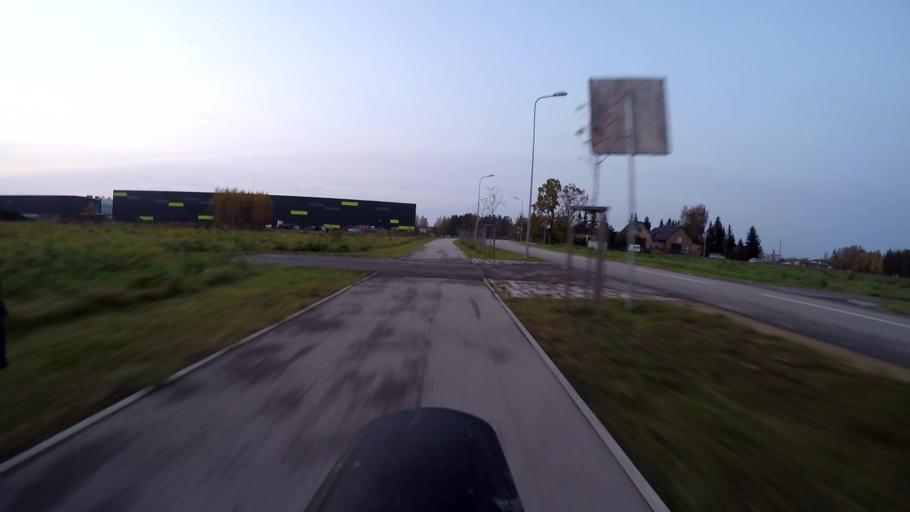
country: LV
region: Marupe
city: Marupe
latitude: 56.9158
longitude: 23.9925
